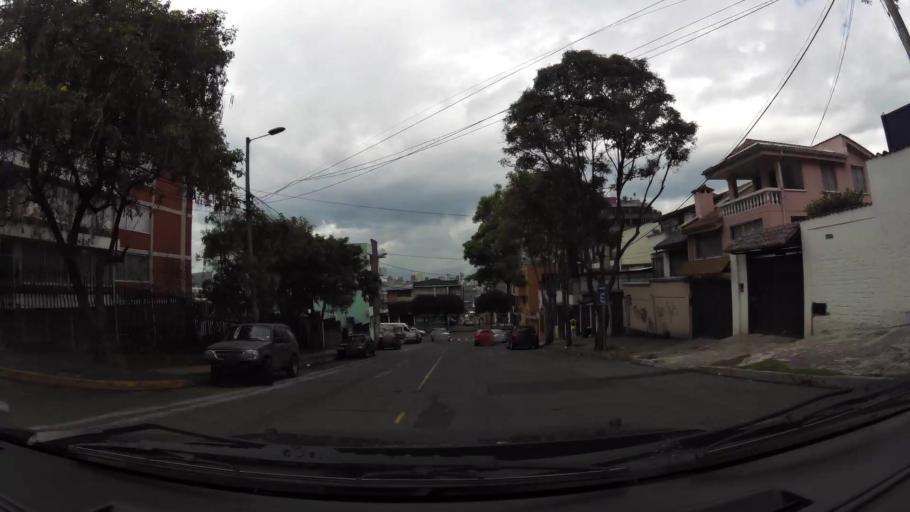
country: EC
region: Pichincha
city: Quito
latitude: -0.1885
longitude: -78.4969
